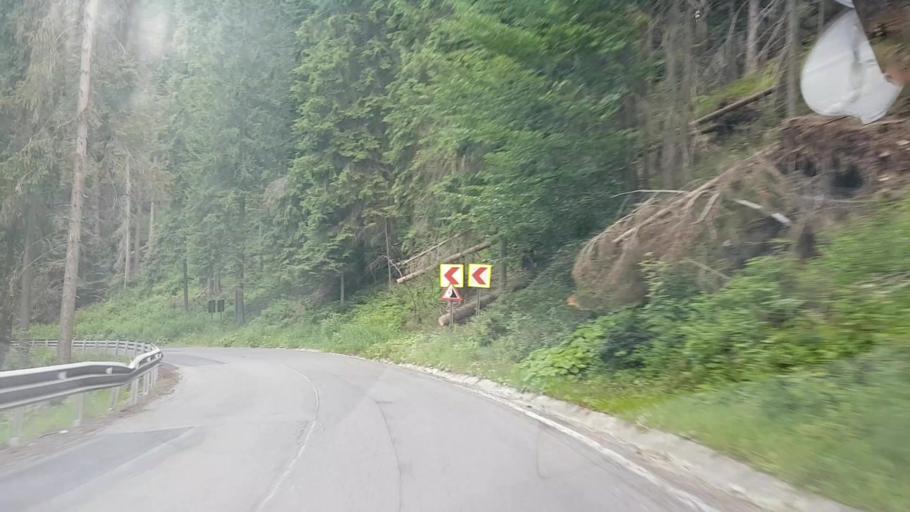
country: RO
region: Harghita
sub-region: Comuna Varsag
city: Varsag
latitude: 46.6427
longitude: 25.2818
